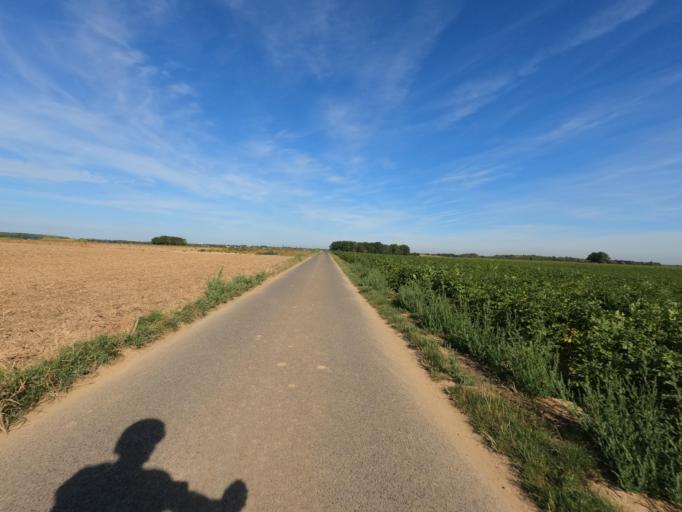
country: DE
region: North Rhine-Westphalia
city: Erkelenz
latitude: 51.0454
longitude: 6.3672
